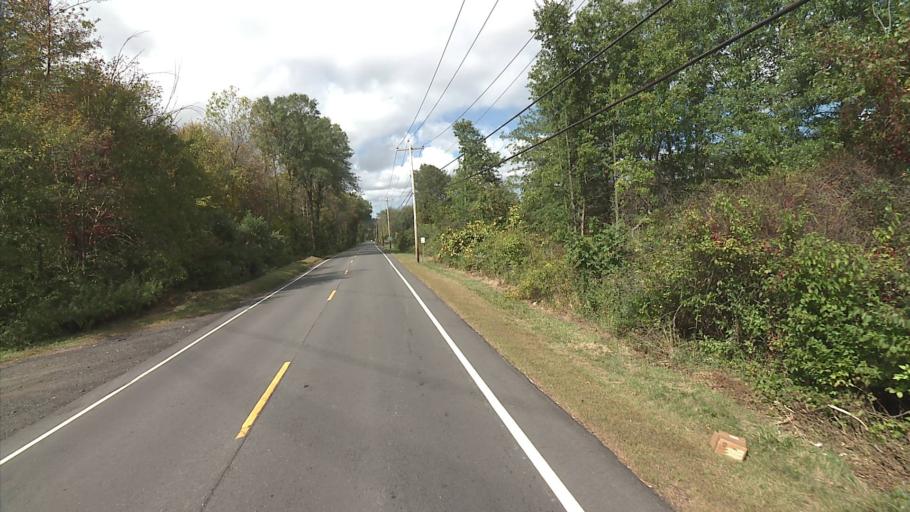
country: US
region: Connecticut
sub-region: Middlesex County
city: Durham
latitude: 41.4927
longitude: -72.6957
